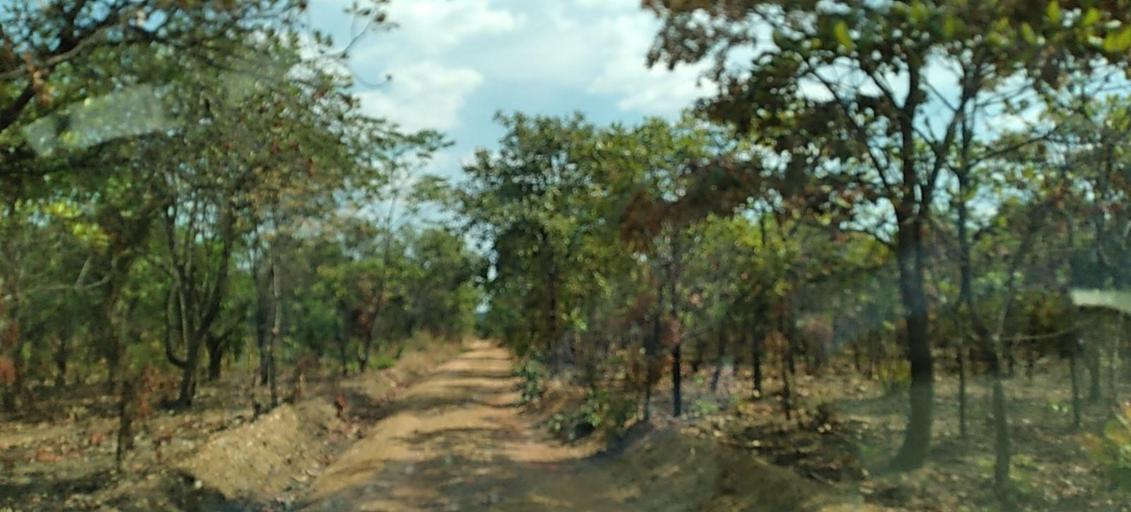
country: ZM
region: Copperbelt
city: Chililabombwe
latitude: -12.3235
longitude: 27.7878
